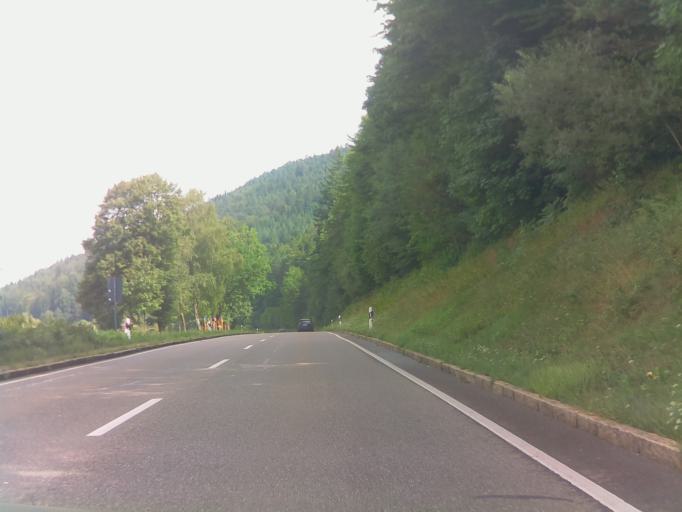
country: DE
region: Baden-Wuerttemberg
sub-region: Karlsruhe Region
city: Bad Herrenalb
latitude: 48.8143
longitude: 8.4449
